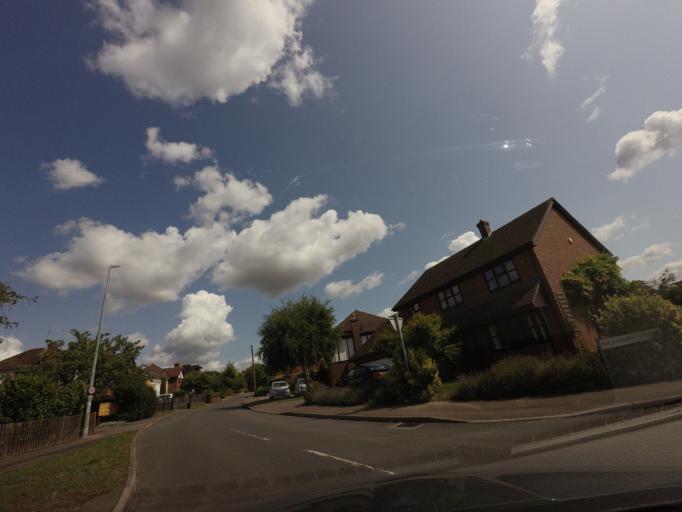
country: GB
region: England
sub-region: Kent
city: Boxley
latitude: 51.2720
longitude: 0.5534
